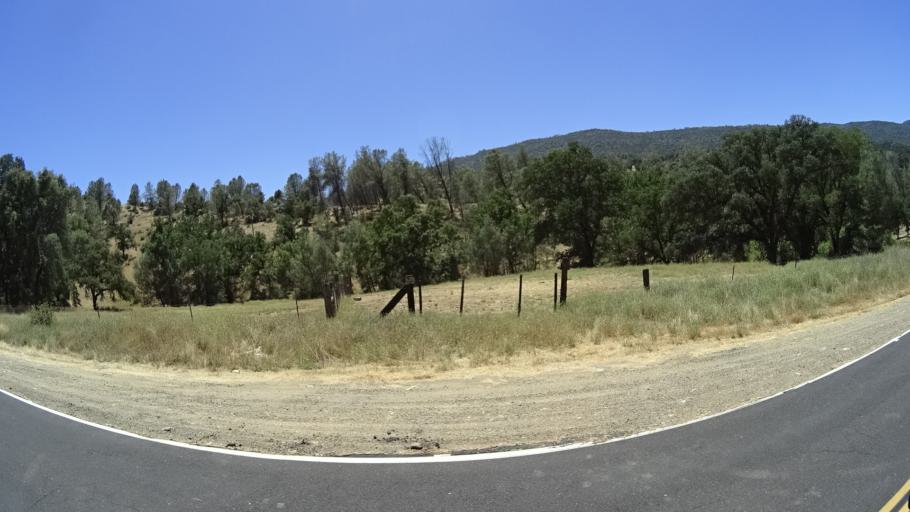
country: US
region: California
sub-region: Calaveras County
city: San Andreas
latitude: 38.1551
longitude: -120.6659
